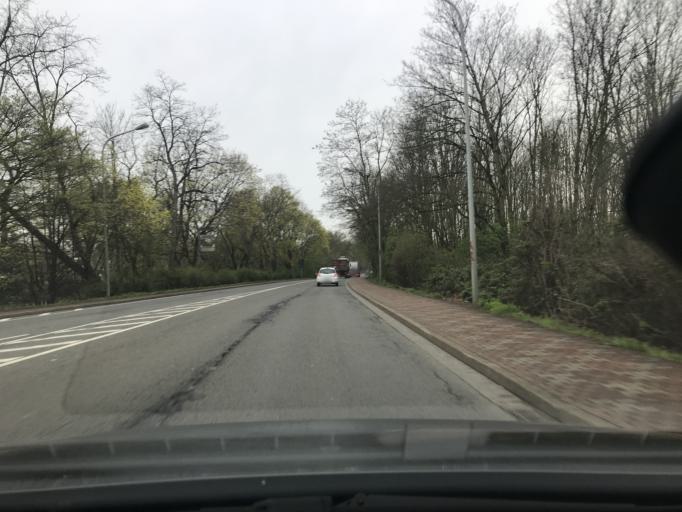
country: DE
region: North Rhine-Westphalia
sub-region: Regierungsbezirk Dusseldorf
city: Krefeld
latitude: 51.3512
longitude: 6.6384
